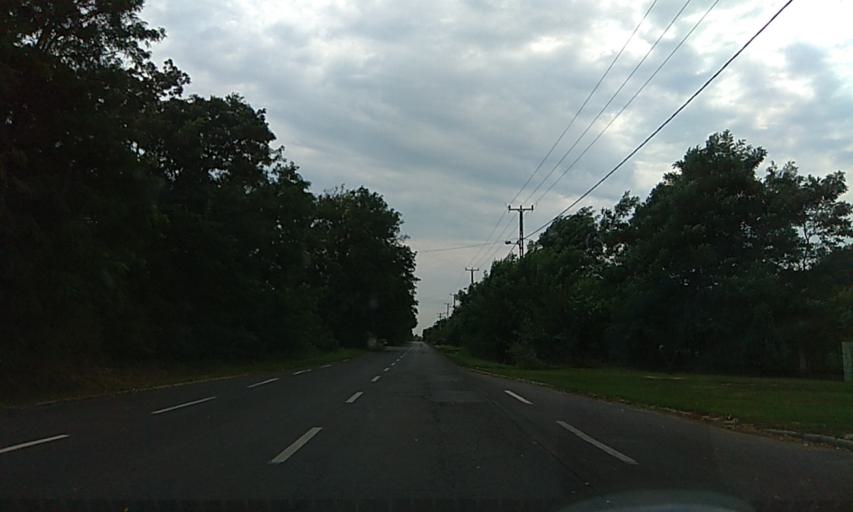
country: HU
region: Szabolcs-Szatmar-Bereg
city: Kotaj
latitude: 48.0225
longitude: 21.6817
